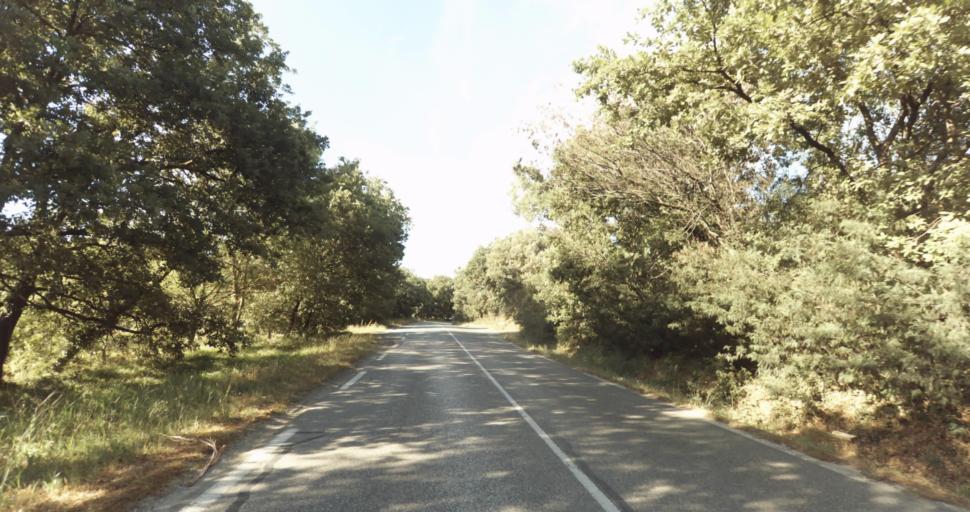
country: FR
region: Provence-Alpes-Cote d'Azur
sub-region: Departement du Var
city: Gassin
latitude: 43.2263
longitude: 6.5721
